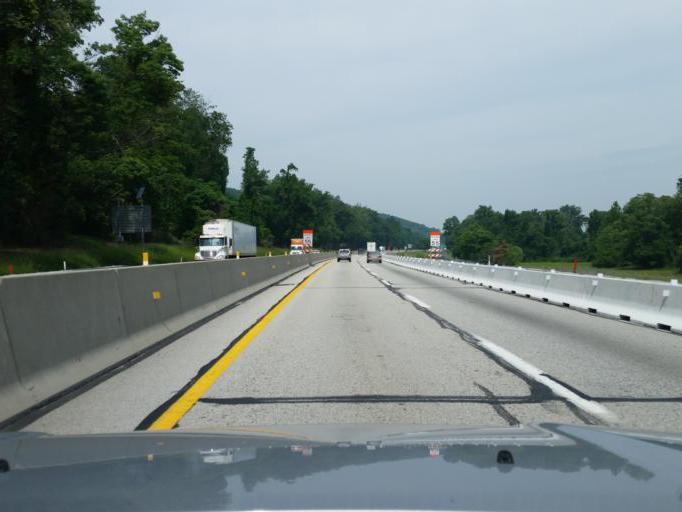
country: US
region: Pennsylvania
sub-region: Dauphin County
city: Bressler
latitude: 40.1975
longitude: -76.8299
